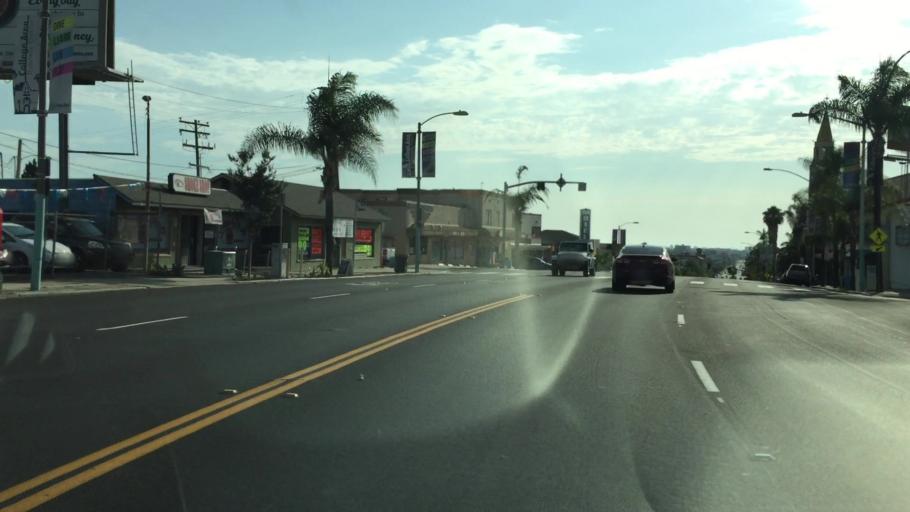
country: US
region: California
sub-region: San Diego County
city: Lemon Grove
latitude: 32.7589
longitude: -117.0724
